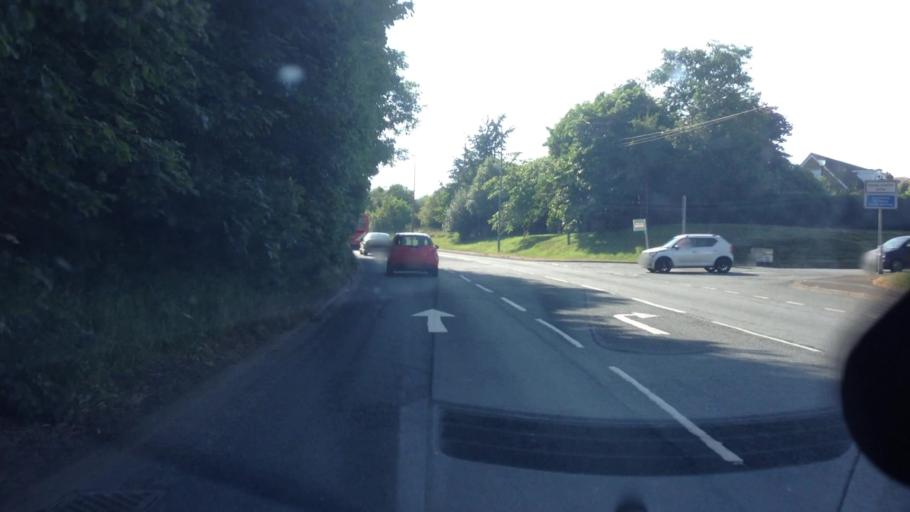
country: GB
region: England
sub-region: Calderdale
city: Elland
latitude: 53.6700
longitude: -1.8296
